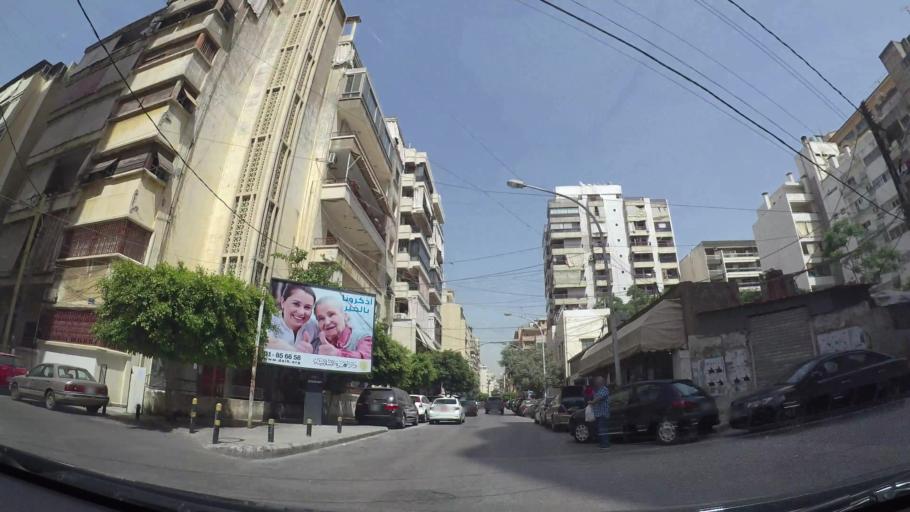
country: LB
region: Beyrouth
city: Ra's Bayrut
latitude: 33.8937
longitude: 35.4783
